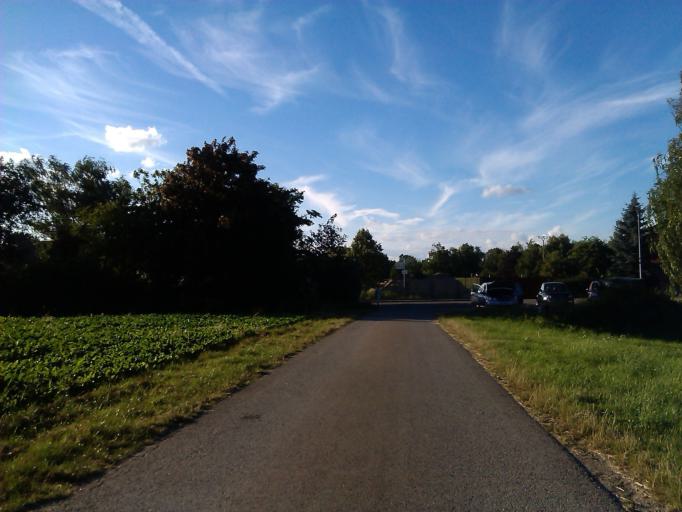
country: DE
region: Rheinland-Pfalz
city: Otterstadt
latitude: 49.3713
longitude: 8.4608
